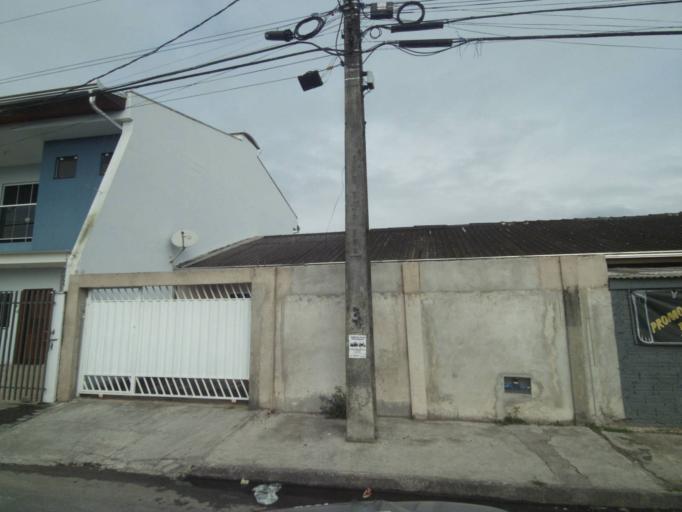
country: BR
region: Parana
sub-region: Paranagua
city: Paranagua
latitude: -25.5649
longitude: -48.5646
